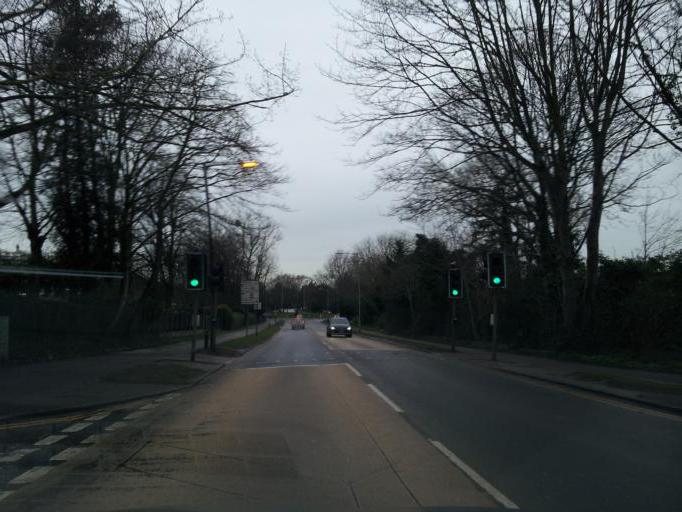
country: GB
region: England
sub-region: Cambridgeshire
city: Cambridge
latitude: 52.1751
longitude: 0.1473
